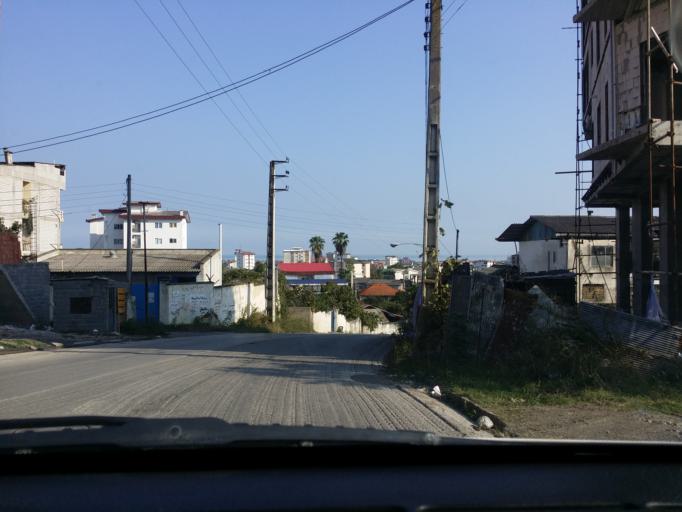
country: IR
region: Mazandaran
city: Chalus
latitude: 36.6460
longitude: 51.4263
